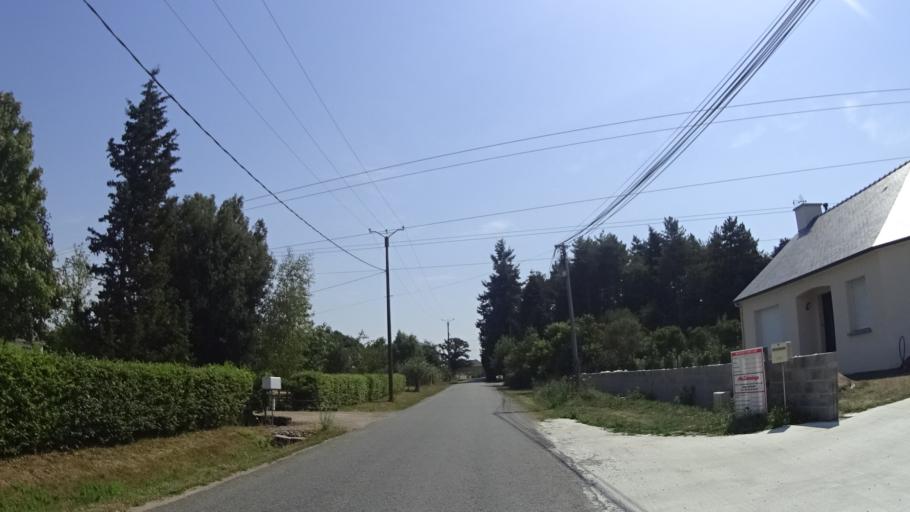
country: FR
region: Pays de la Loire
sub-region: Departement de la Loire-Atlantique
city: Prinquiau
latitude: 47.3498
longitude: -2.0003
